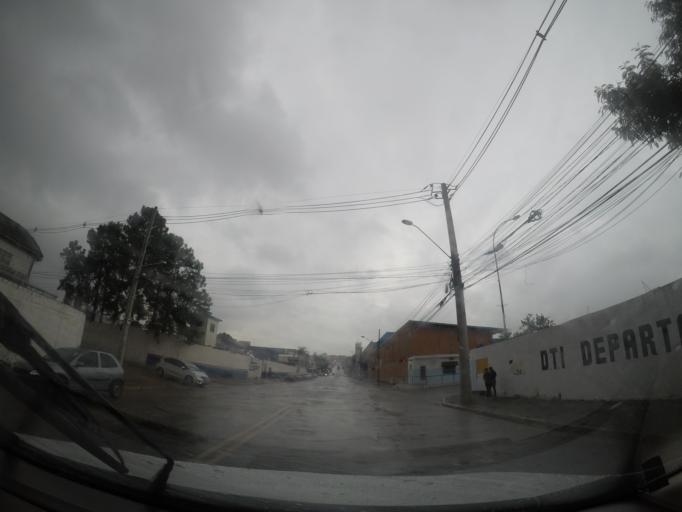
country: BR
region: Sao Paulo
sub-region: Guarulhos
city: Guarulhos
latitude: -23.4405
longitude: -46.5016
